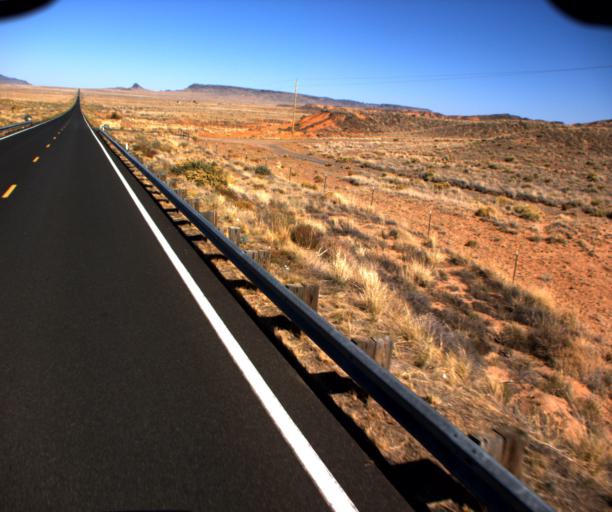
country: US
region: Arizona
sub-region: Navajo County
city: Dilkon
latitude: 35.3219
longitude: -110.4231
